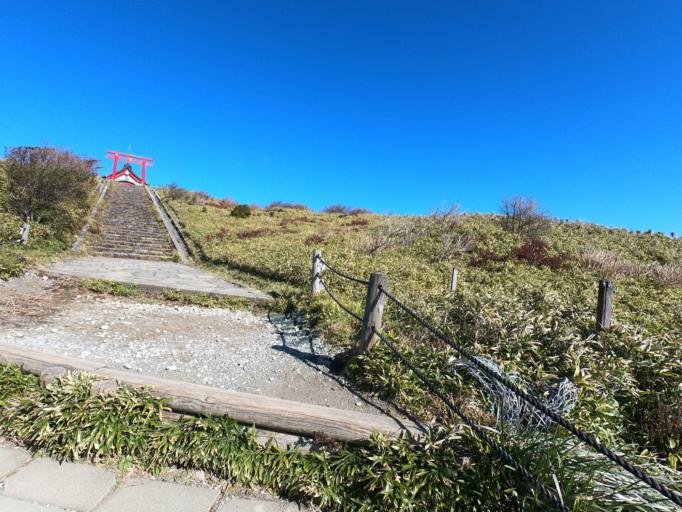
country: JP
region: Kanagawa
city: Hakone
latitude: 35.2242
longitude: 139.0255
